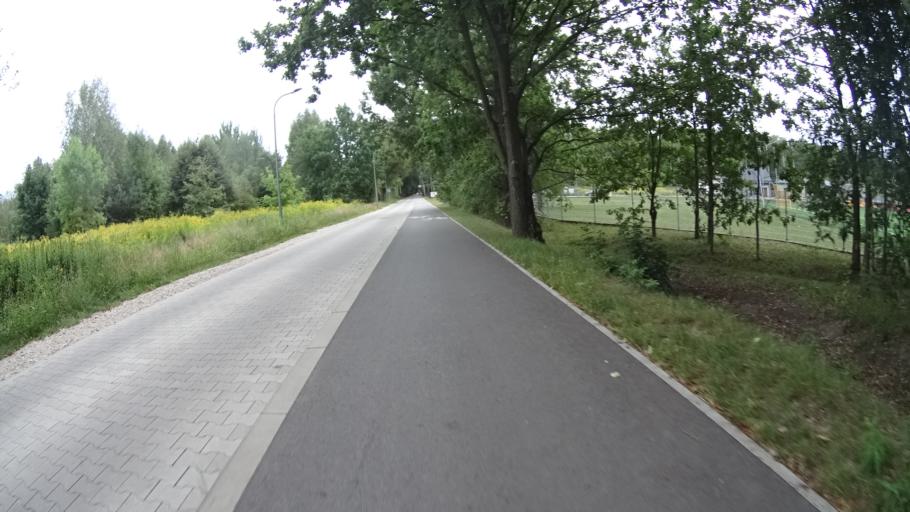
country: PL
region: Masovian Voivodeship
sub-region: Powiat pruszkowski
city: Granica
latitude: 52.1333
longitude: 20.8007
